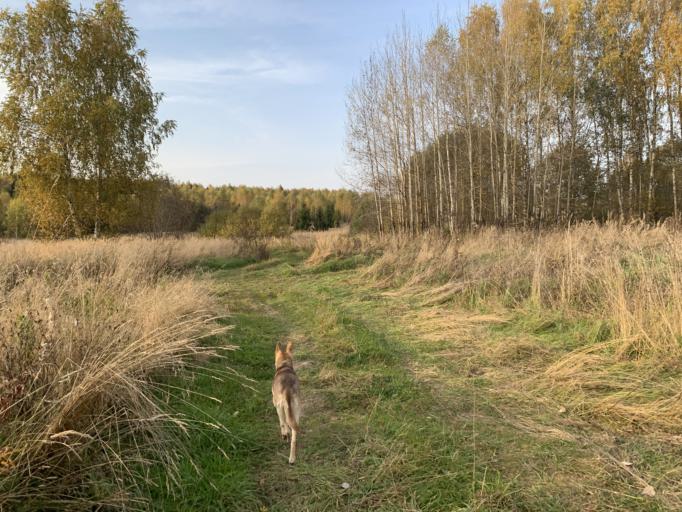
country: RU
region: Jaroslavl
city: Porech'ye-Rybnoye
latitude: 56.9871
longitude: 39.3847
